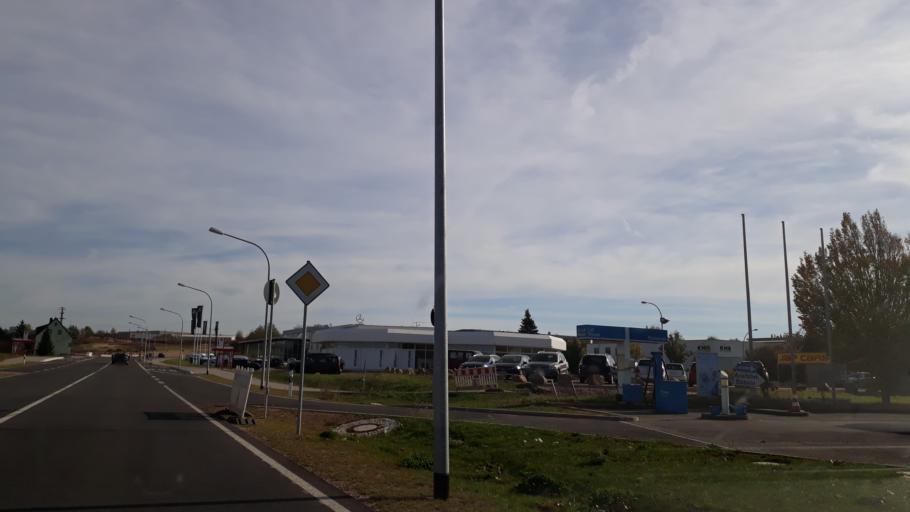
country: DE
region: Saxony
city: Mochau
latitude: 51.1207
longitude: 13.1502
